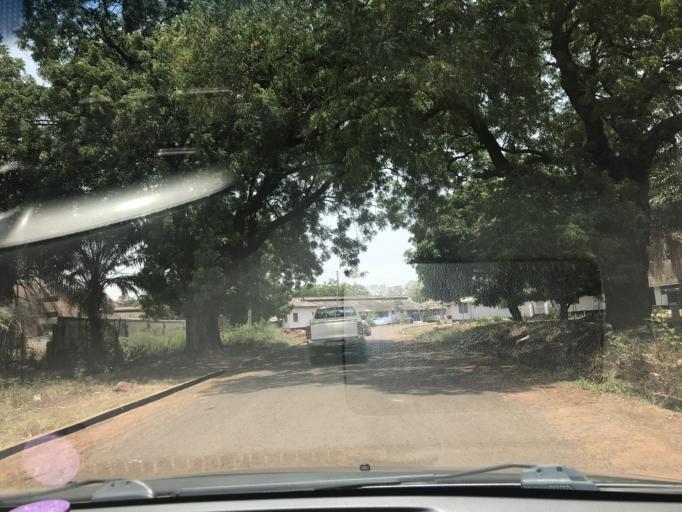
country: GH
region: Greater Accra
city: Teshi Old Town
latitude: 5.5845
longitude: -0.1539
